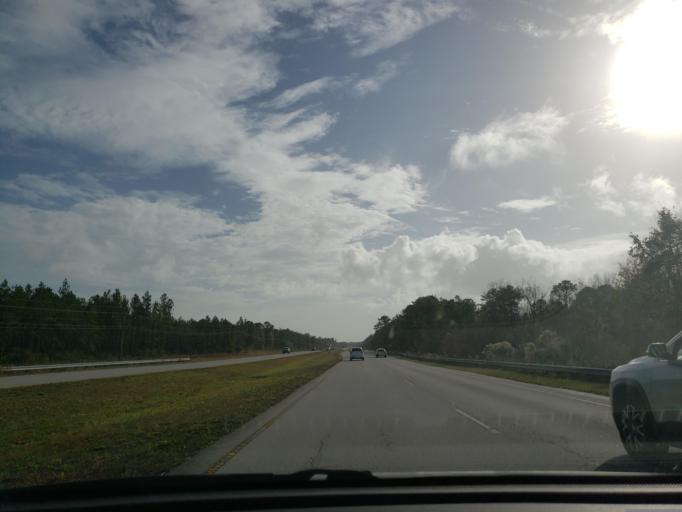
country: US
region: North Carolina
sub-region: Onslow County
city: Sneads Ferry
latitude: 34.6326
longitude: -77.4808
